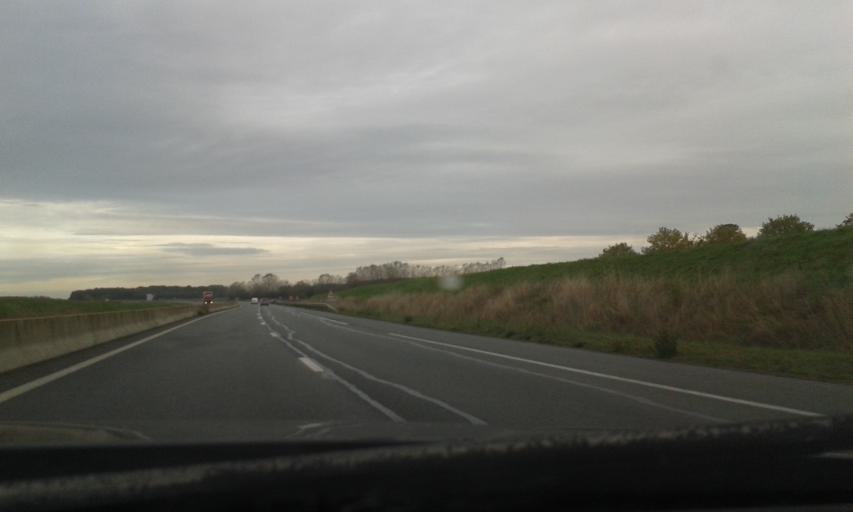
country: FR
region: Centre
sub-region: Departement d'Eure-et-Loir
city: Vernouillet
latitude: 48.6764
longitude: 1.3831
